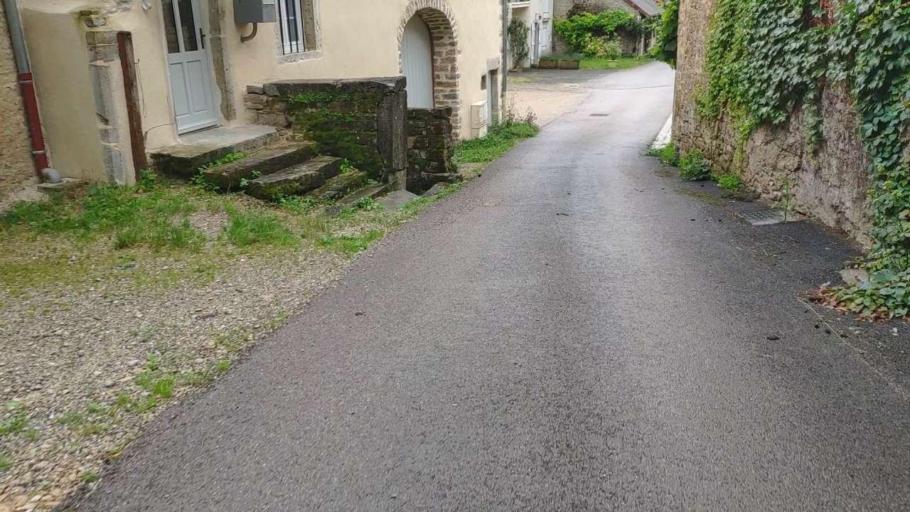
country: FR
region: Franche-Comte
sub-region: Departement du Jura
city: Poligny
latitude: 46.7839
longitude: 5.6174
